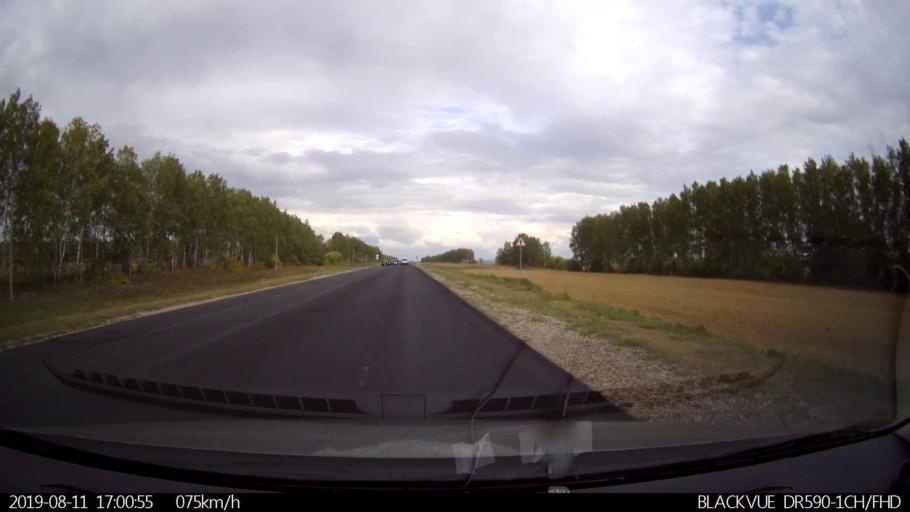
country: RU
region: Ulyanovsk
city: Mayna
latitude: 54.3093
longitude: 47.6877
